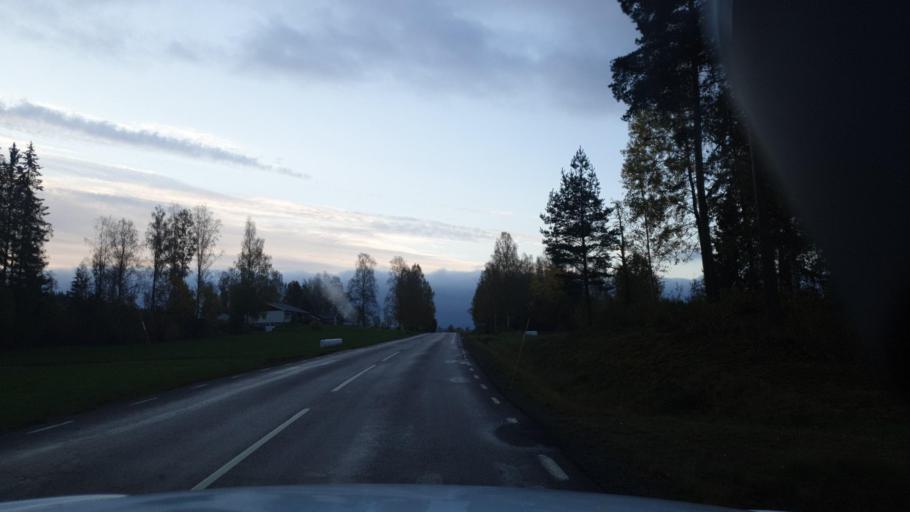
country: SE
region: Vaermland
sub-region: Arvika Kommun
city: Arvika
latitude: 59.8059
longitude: 12.6009
